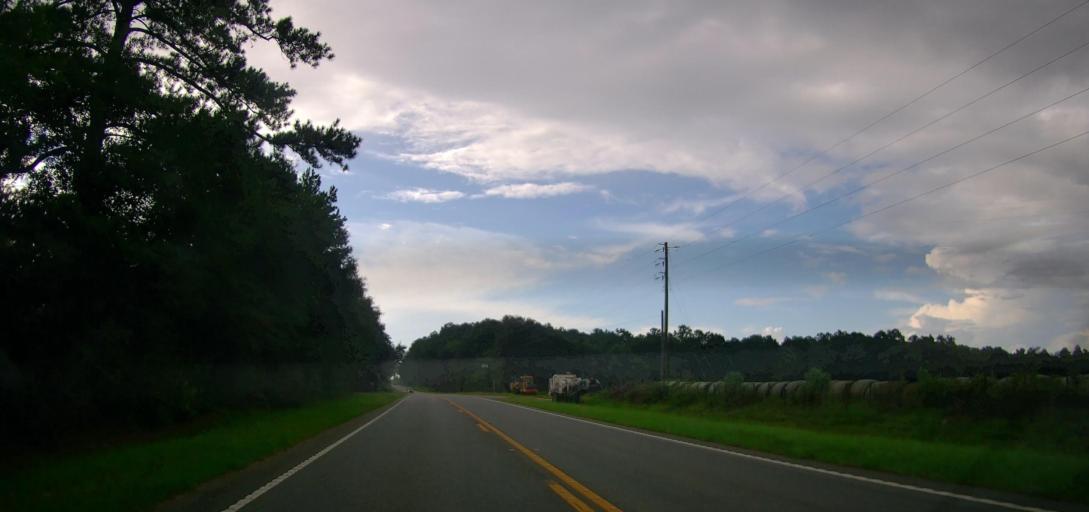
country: US
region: Georgia
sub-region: Ware County
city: Deenwood
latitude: 31.3089
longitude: -82.5655
